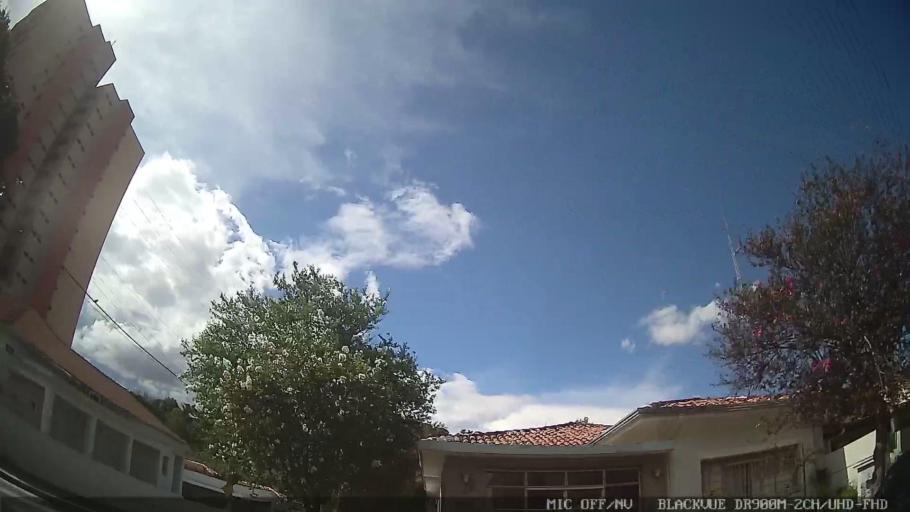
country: BR
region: Sao Paulo
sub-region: Pedreira
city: Pedreira
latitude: -22.7420
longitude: -46.9018
